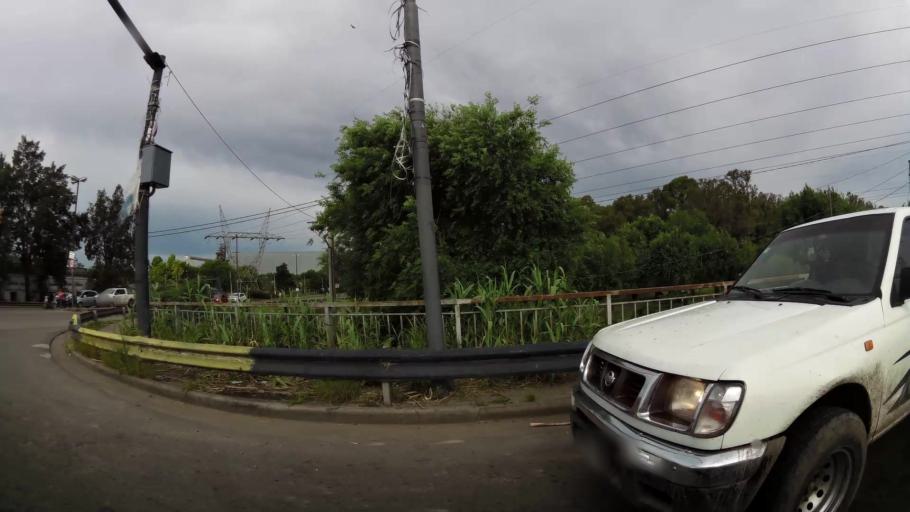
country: AR
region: Santa Fe
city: Gobernador Galvez
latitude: -32.9922
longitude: -60.6887
